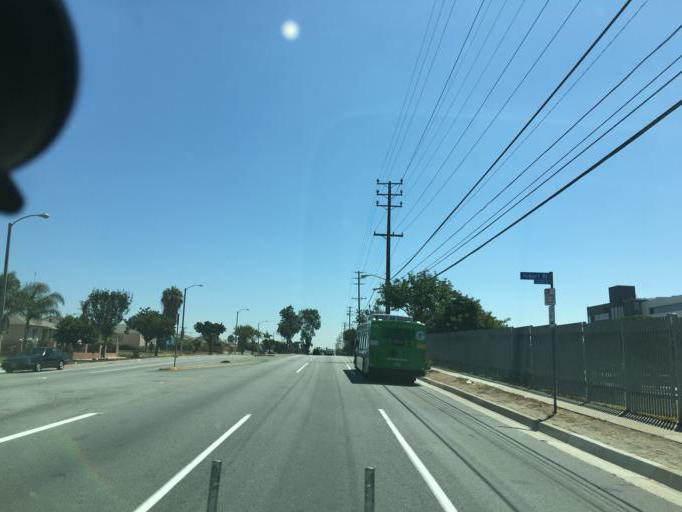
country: US
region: California
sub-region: Los Angeles County
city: West Athens
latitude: 33.9309
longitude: -118.3076
